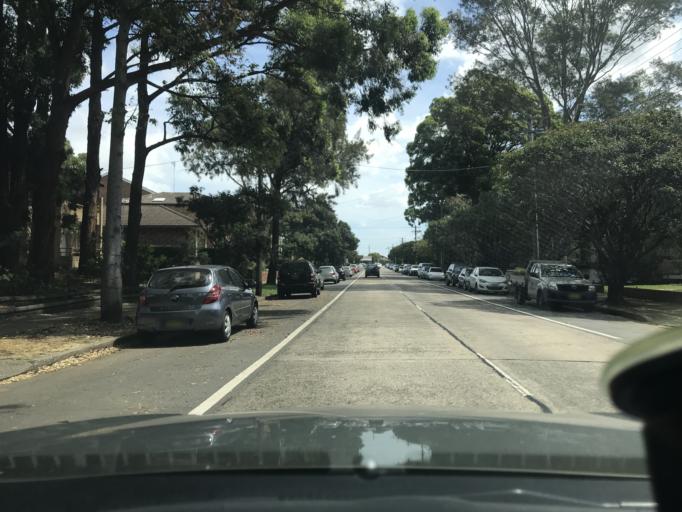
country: AU
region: New South Wales
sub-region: Canada Bay
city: Wareemba
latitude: -33.8551
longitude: 151.1336
